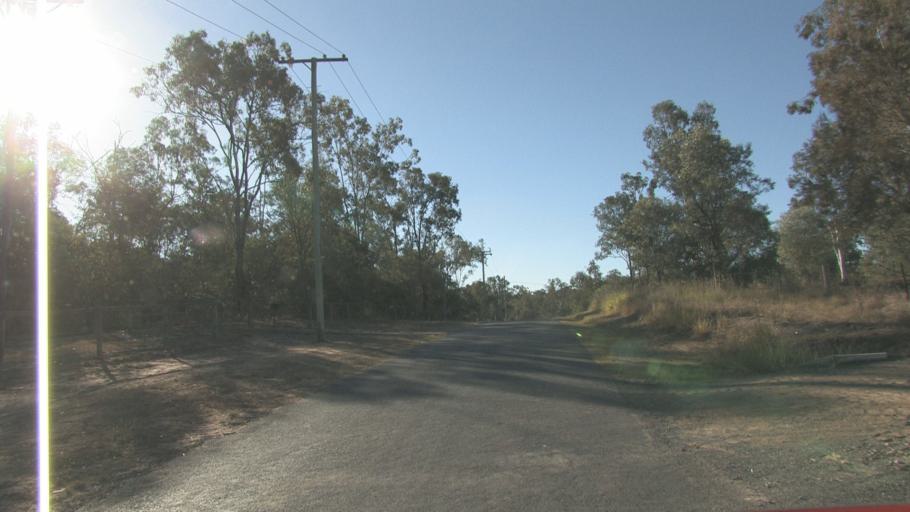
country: AU
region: Queensland
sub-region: Logan
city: North Maclean
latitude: -27.8116
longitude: 153.0411
